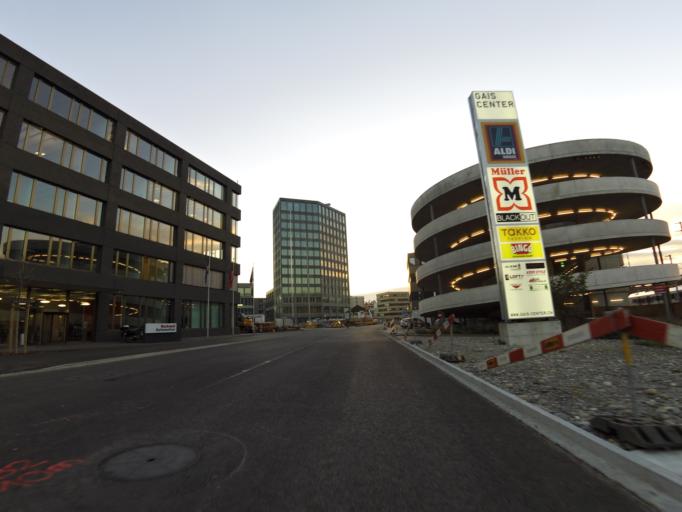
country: CH
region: Aargau
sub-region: Bezirk Aarau
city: Aarau
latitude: 47.3928
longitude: 8.0597
